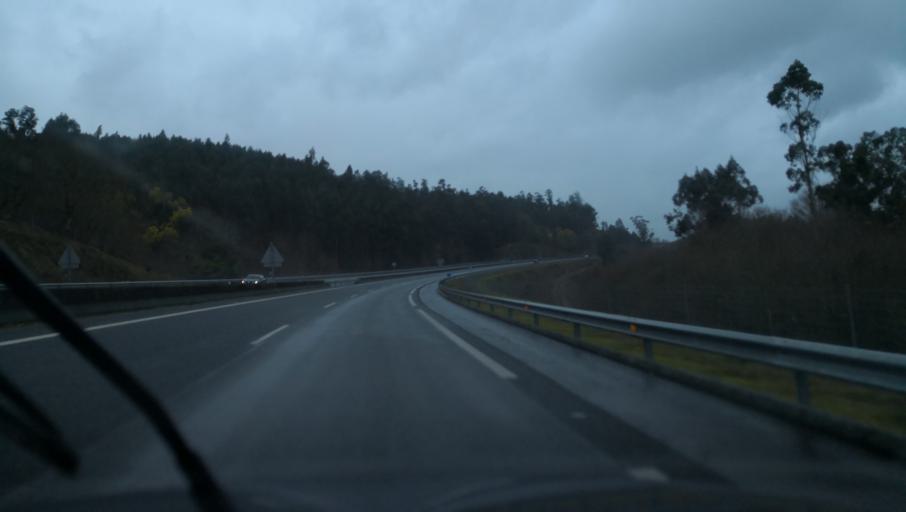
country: ES
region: Galicia
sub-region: Provincia da Coruna
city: Santiago de Compostela
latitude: 42.8297
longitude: -8.5257
